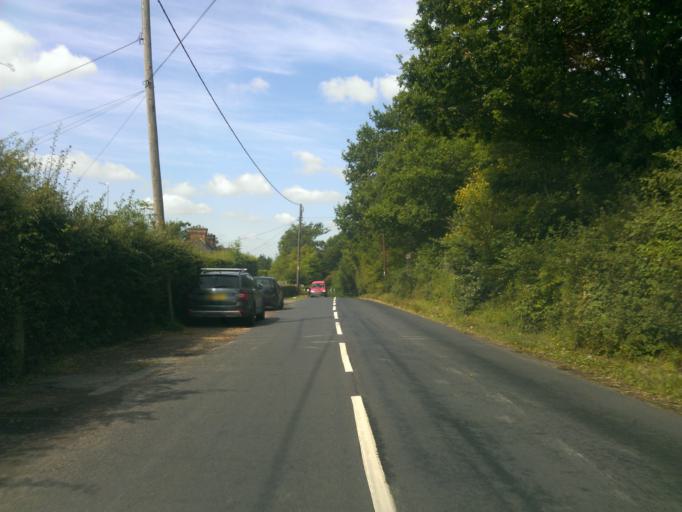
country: GB
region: England
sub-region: Kent
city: Edenbridge
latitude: 51.2017
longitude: 0.1243
